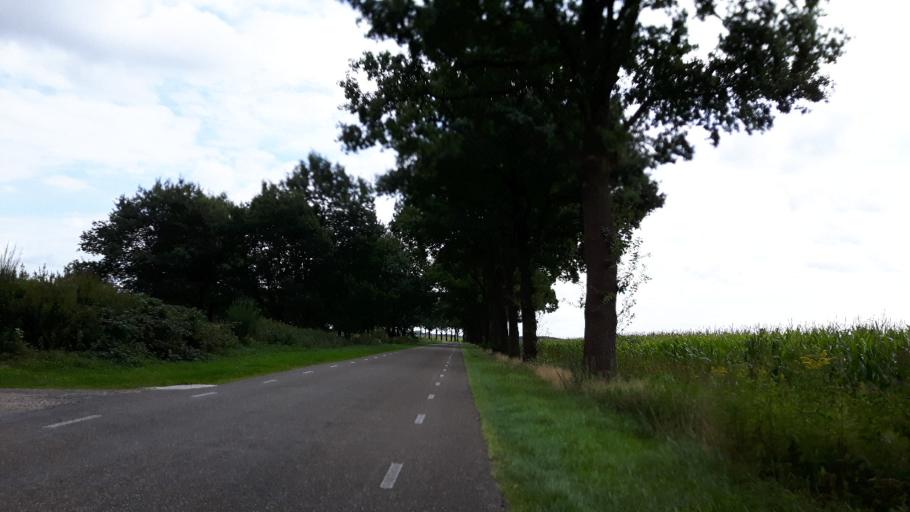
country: NL
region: Groningen
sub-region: Gemeente Leek
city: Leek
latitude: 53.0842
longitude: 6.3520
